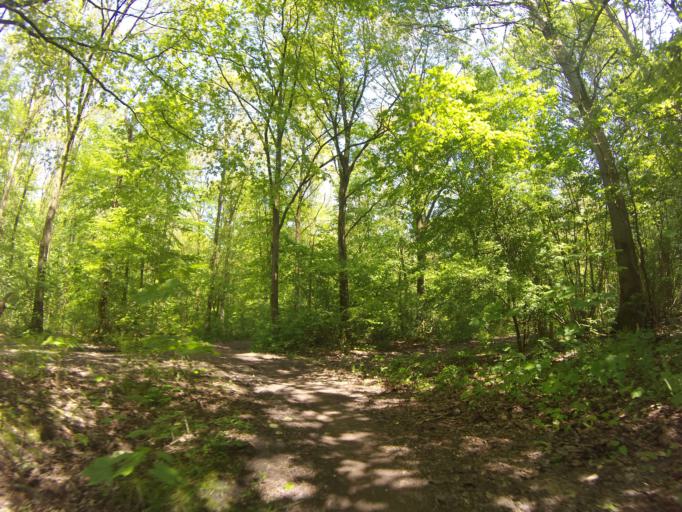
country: NL
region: Flevoland
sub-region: Gemeente Zeewolde
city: Zeewolde
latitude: 52.3076
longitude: 5.5193
